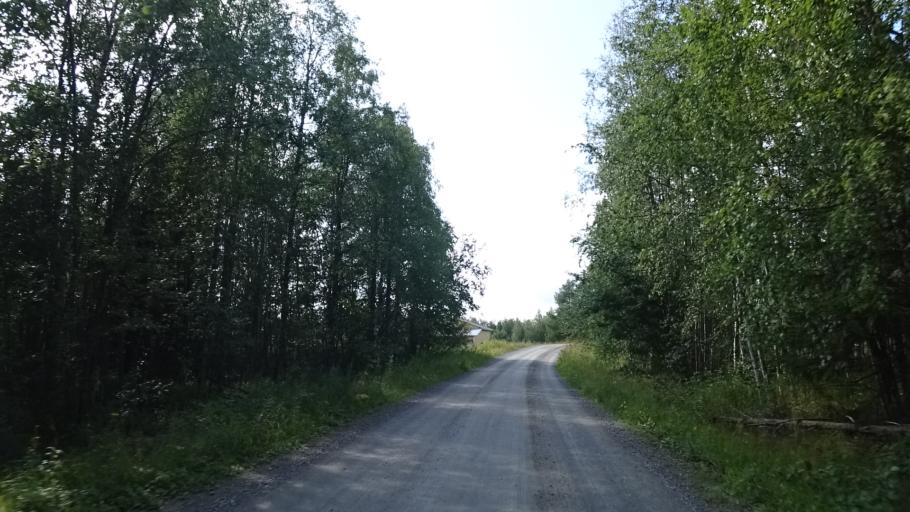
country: FI
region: North Karelia
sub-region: Joensuu
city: Ilomantsi
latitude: 62.9337
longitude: 31.3020
